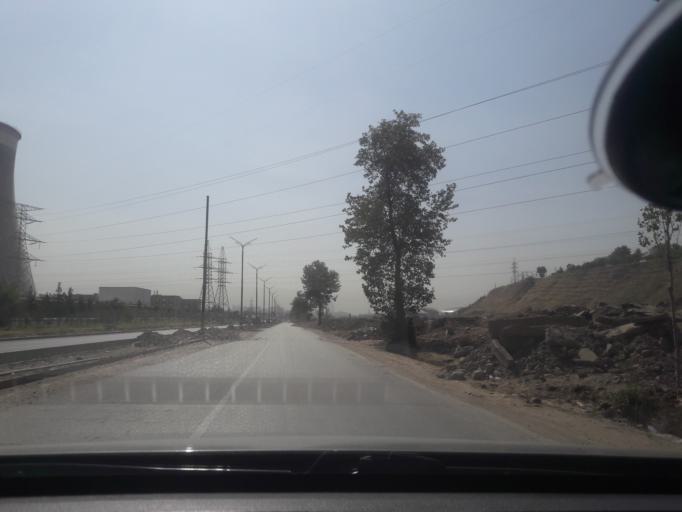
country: TJ
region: Dushanbe
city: Dushanbe
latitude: 38.6101
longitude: 68.7707
